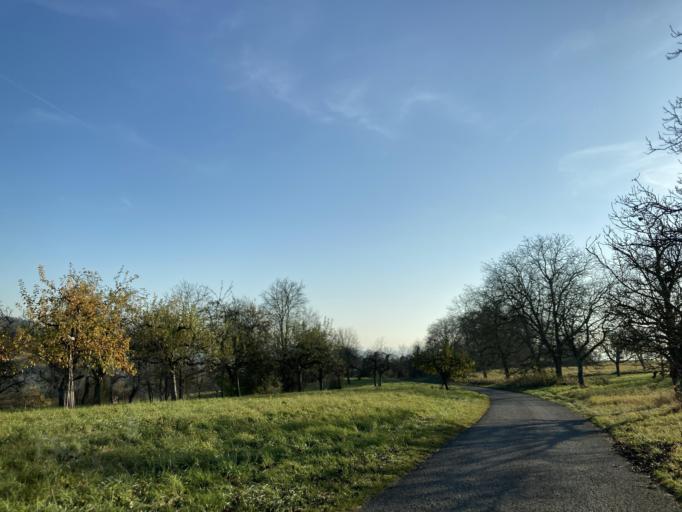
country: DE
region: Baden-Wuerttemberg
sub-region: Tuebingen Region
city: Rottenburg
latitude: 48.5367
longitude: 8.9744
